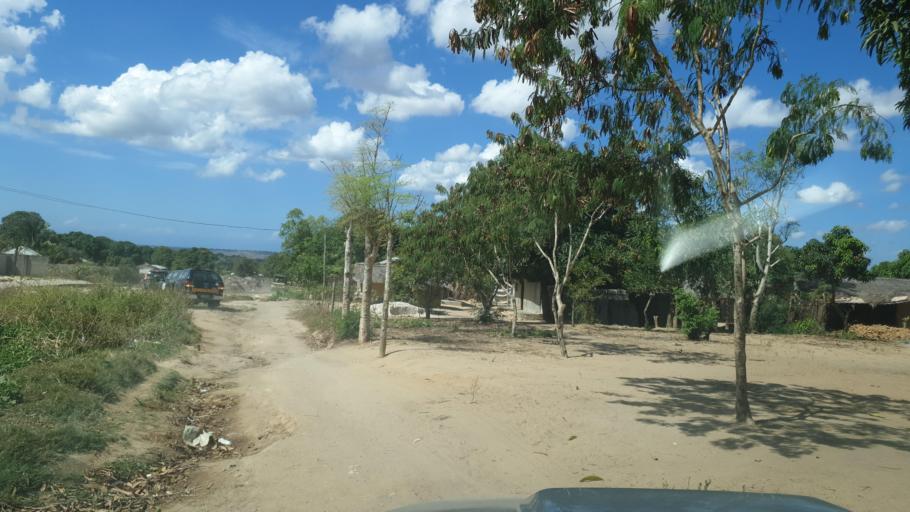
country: MZ
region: Nampula
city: Nacala
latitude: -14.5683
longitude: 40.7048
